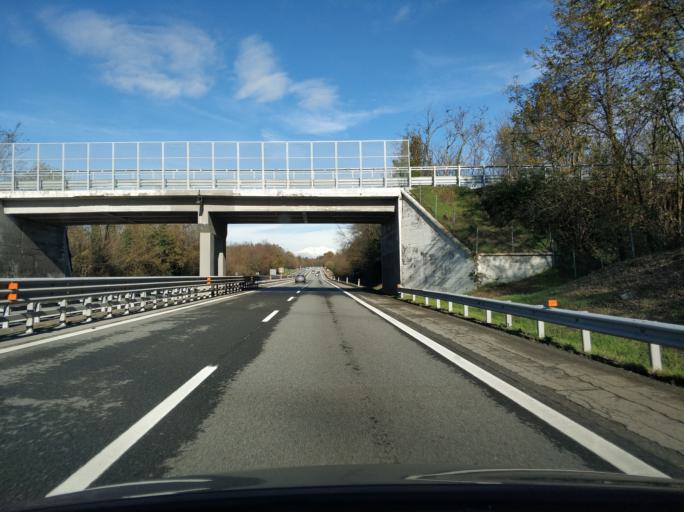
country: IT
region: Piedmont
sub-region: Provincia di Torino
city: Montalenghe
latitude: 45.3337
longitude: 7.8252
